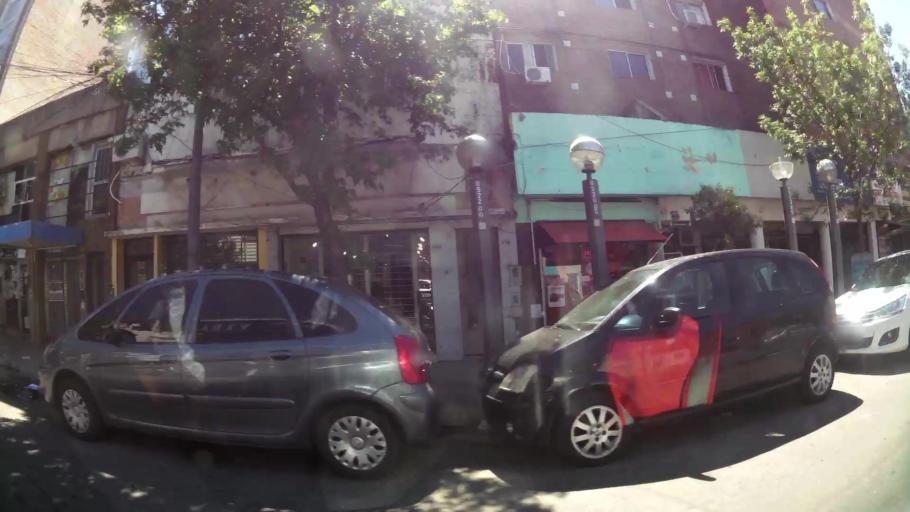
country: AR
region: Santa Fe
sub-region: Departamento de Rosario
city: Rosario
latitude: -32.9374
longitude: -60.6702
